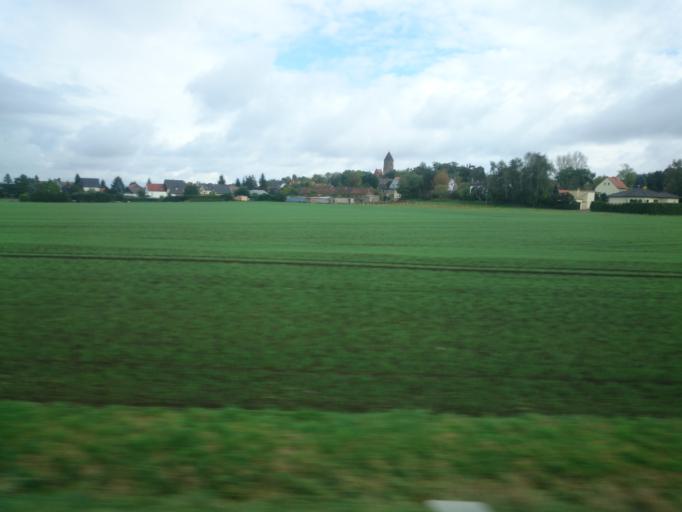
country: DE
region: Saxony-Anhalt
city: Hohenthurm
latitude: 51.5242
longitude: 12.0904
